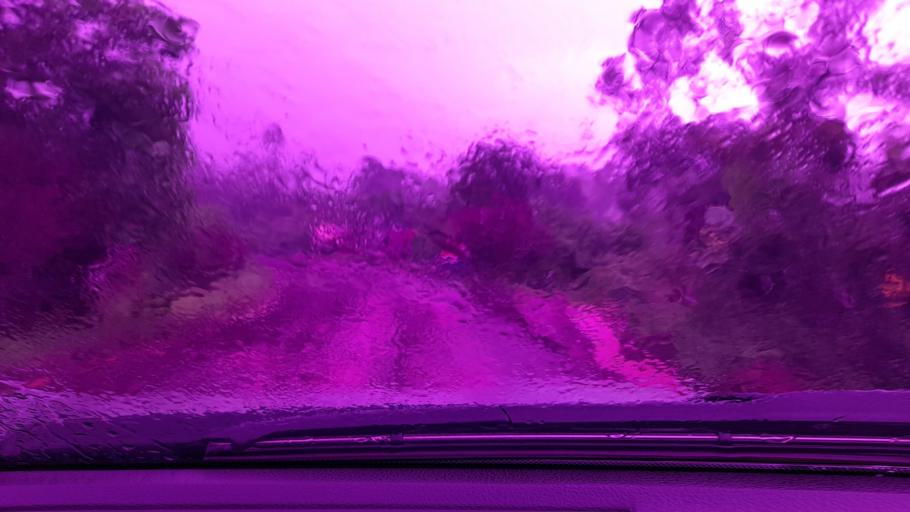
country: ET
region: Oromiya
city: Metu
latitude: 8.3524
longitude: 35.5992
